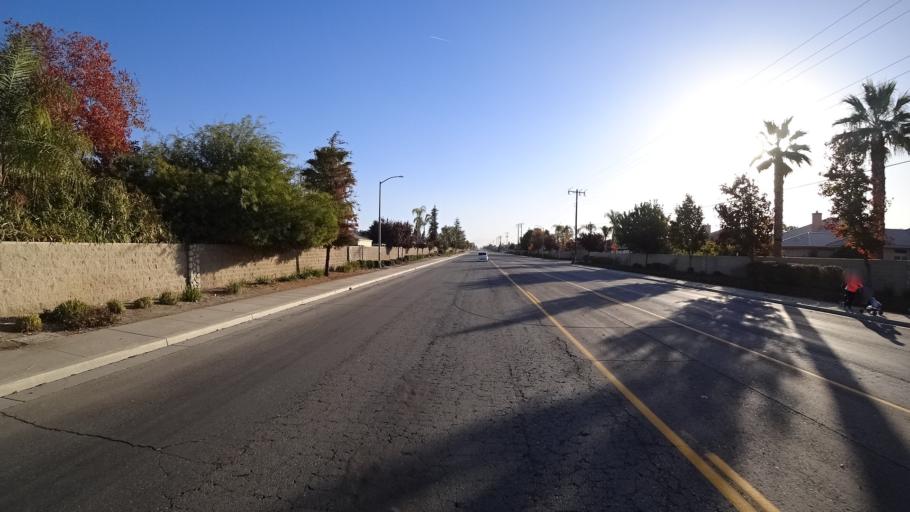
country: US
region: California
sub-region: Kern County
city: Greenfield
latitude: 35.2742
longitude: -119.0508
